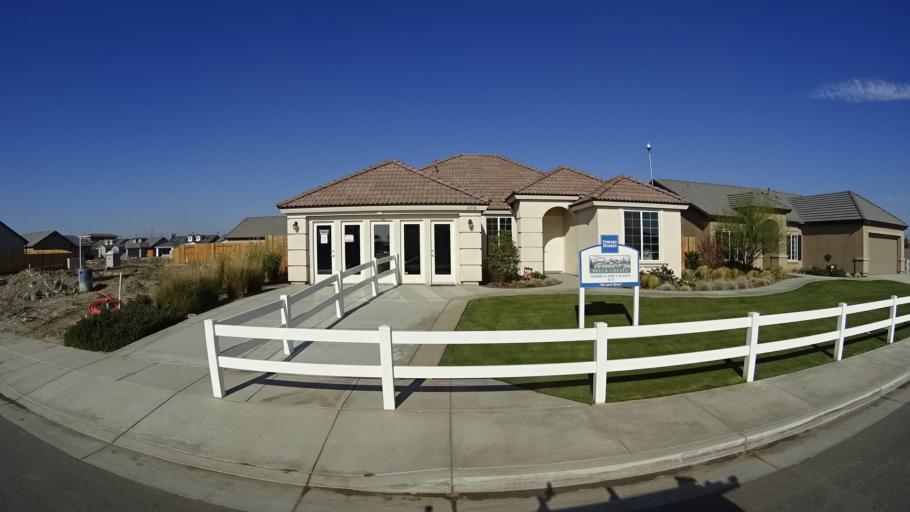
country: US
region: California
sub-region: Kern County
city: Greenfield
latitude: 35.2932
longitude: -119.0754
